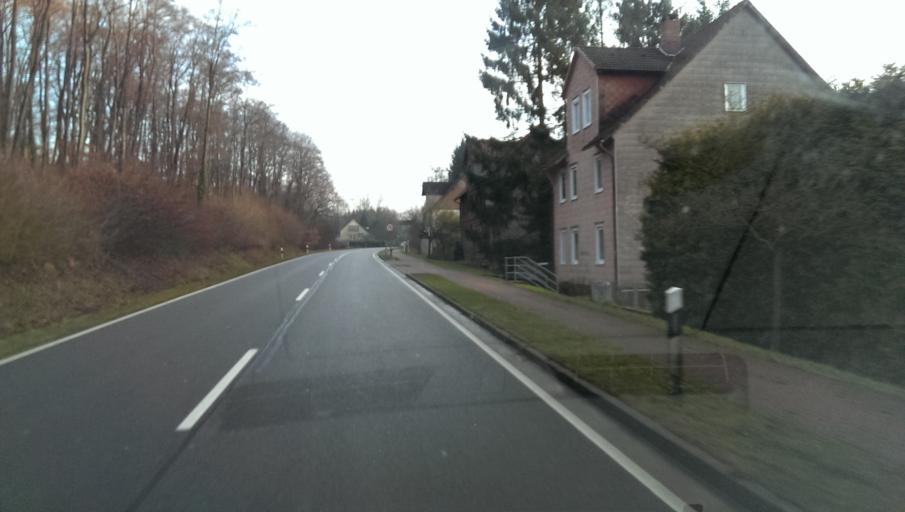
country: DE
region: Lower Saxony
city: Lenne
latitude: 51.8995
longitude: 9.6931
